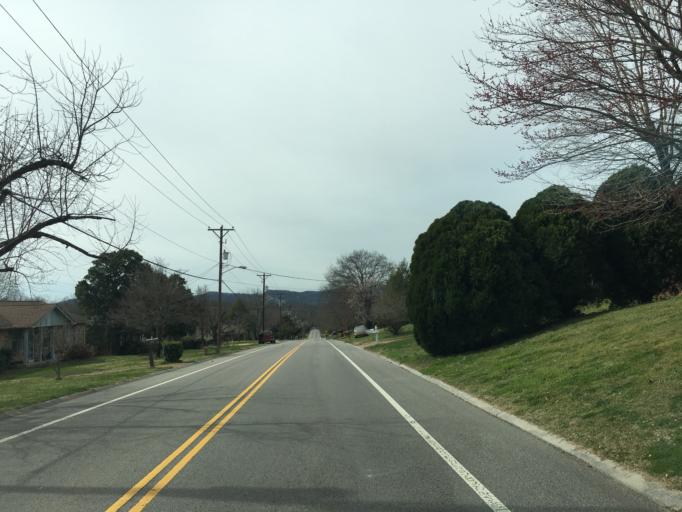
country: US
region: Tennessee
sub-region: Williamson County
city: Brentwood Estates
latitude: 36.0474
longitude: -86.7281
